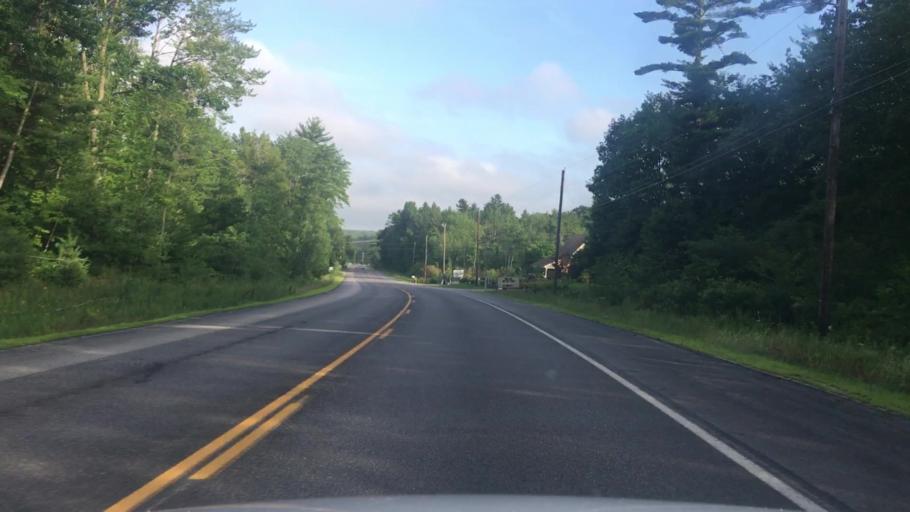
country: US
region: Maine
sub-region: Cumberland County
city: South Windham
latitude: 43.7886
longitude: -70.3960
